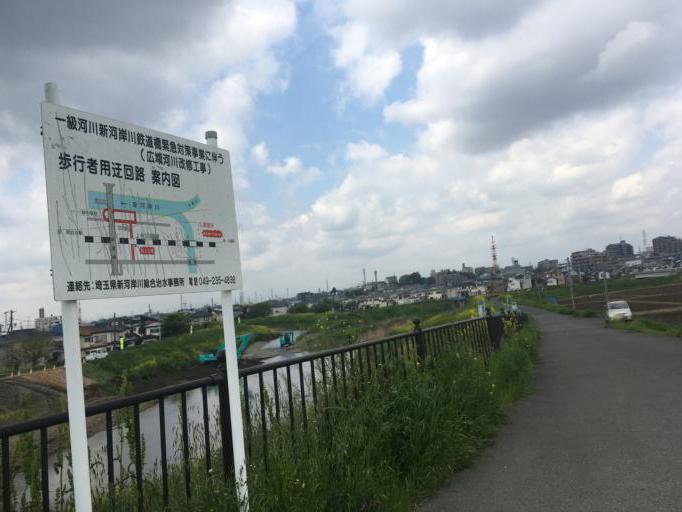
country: JP
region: Saitama
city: Kawagoe
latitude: 35.8990
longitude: 139.4957
